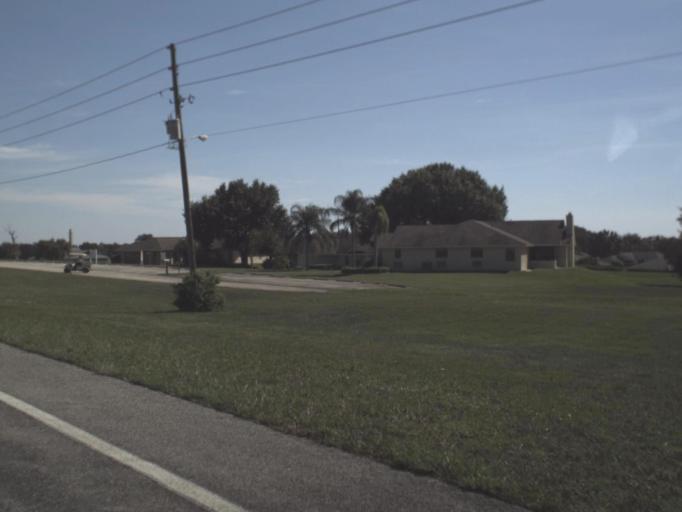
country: US
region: Florida
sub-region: Highlands County
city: Lake Placid
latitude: 27.3246
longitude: -81.3734
